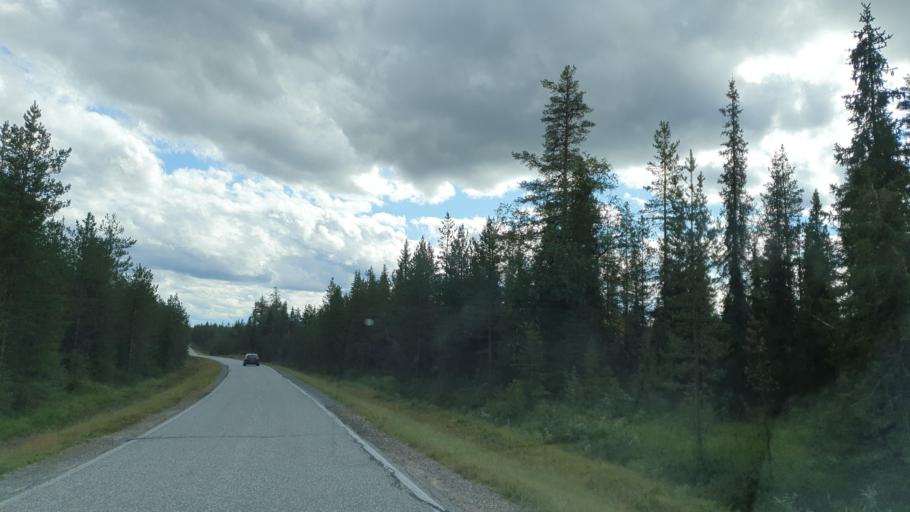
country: FI
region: Lapland
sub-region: Tunturi-Lappi
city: Muonio
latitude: 67.7195
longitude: 24.0764
